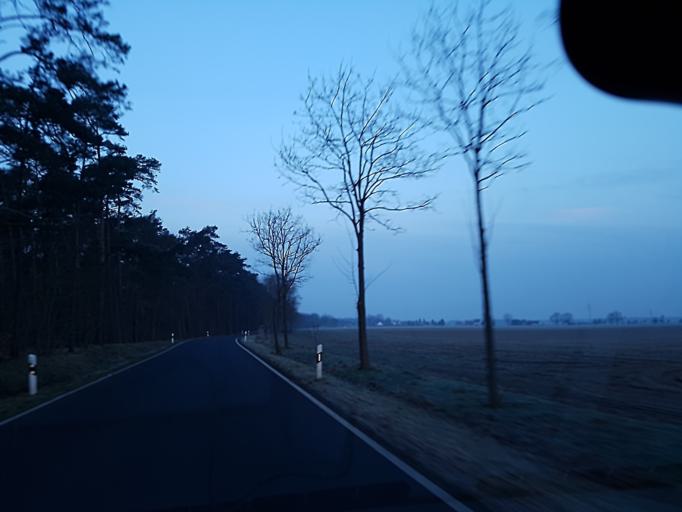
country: DE
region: Brandenburg
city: Herzberg
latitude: 51.7352
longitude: 13.1875
